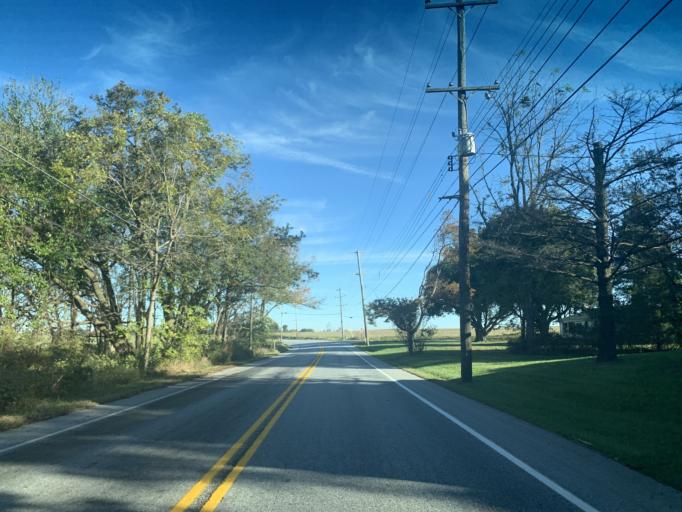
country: US
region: Pennsylvania
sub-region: Chester County
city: Parkesburg
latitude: 39.8755
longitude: -75.9215
